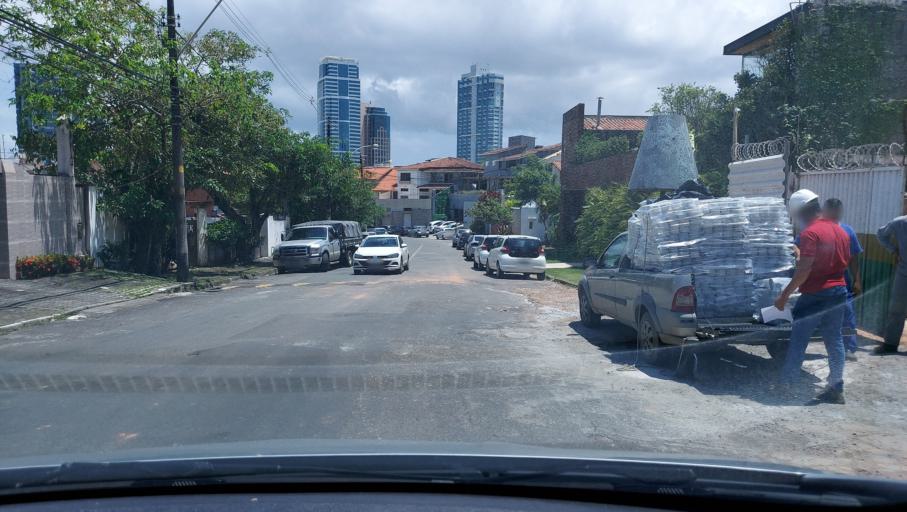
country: BR
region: Bahia
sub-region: Salvador
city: Salvador
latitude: -12.9827
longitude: -38.4567
